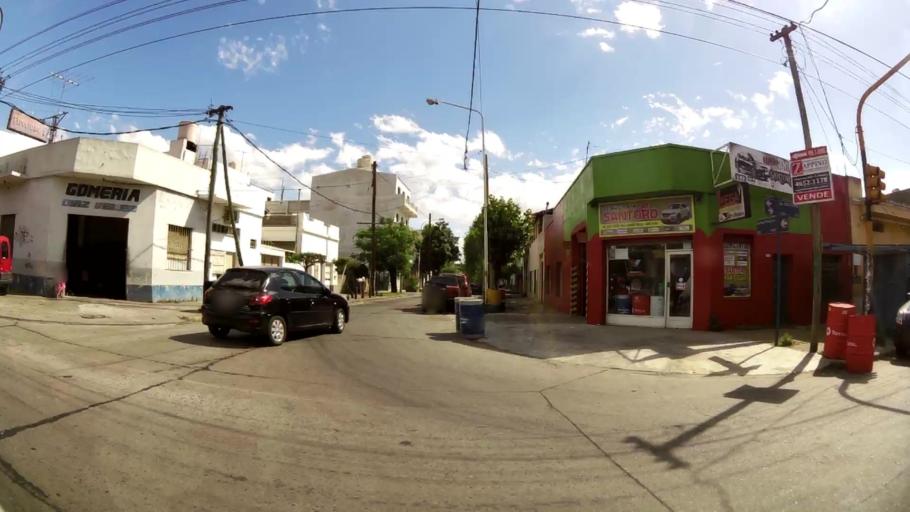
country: AR
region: Buenos Aires
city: San Justo
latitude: -34.6487
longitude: -58.5372
